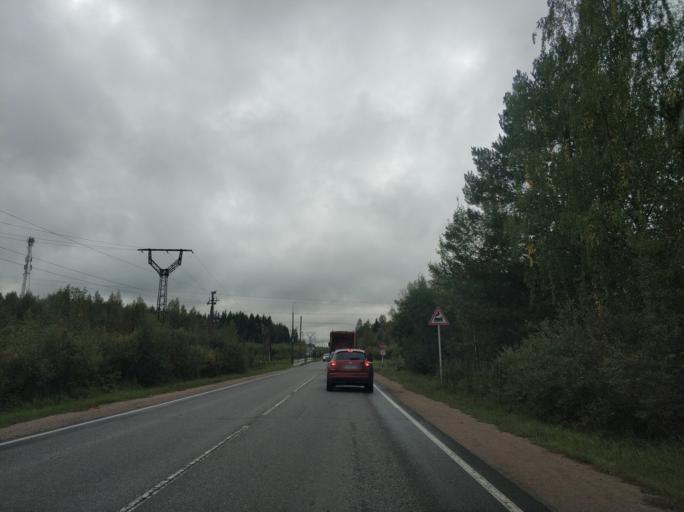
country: RU
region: Leningrad
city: Borisova Griva
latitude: 60.0960
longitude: 30.9533
